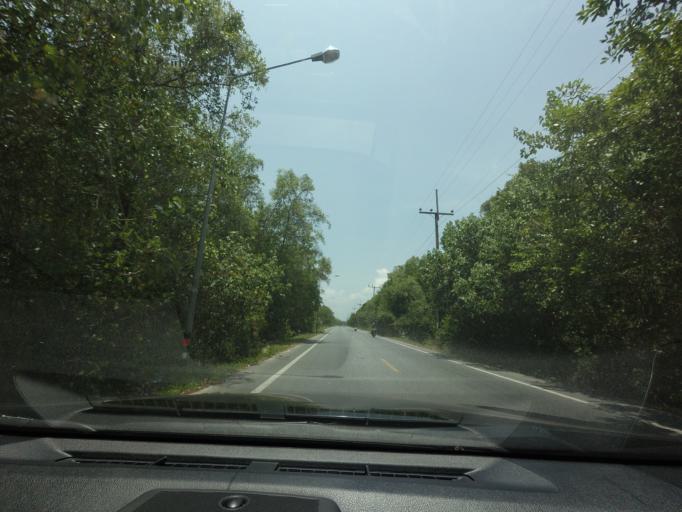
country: TH
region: Pattani
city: Yaring
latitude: 6.8812
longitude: 101.3756
